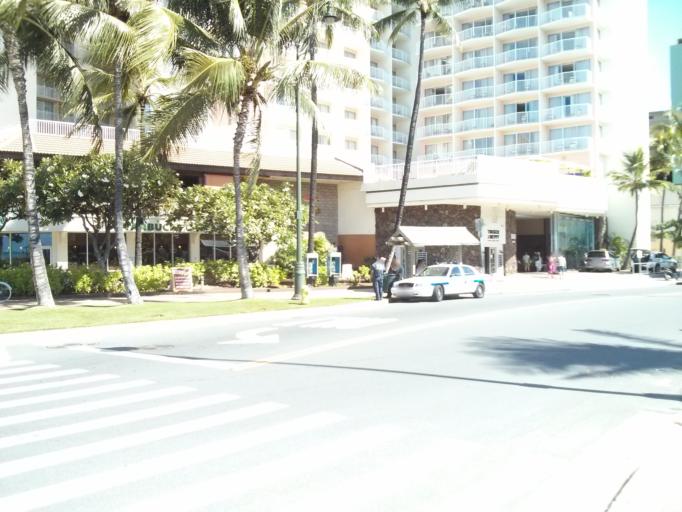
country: US
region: Hawaii
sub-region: Honolulu County
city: Honolulu
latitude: 21.2716
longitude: -157.8226
